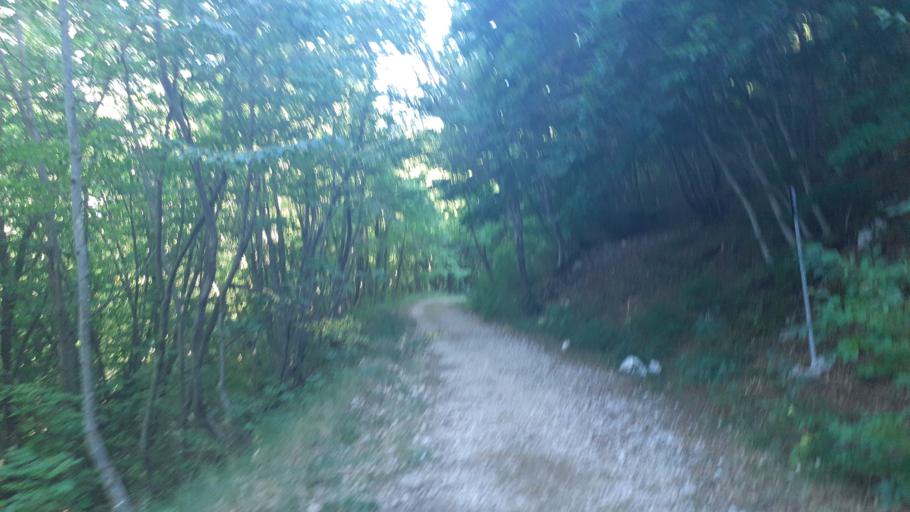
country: IT
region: Abruzzo
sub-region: Provincia di Pescara
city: Sant'Eufemia a Maiella
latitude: 42.1062
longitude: 14.0033
